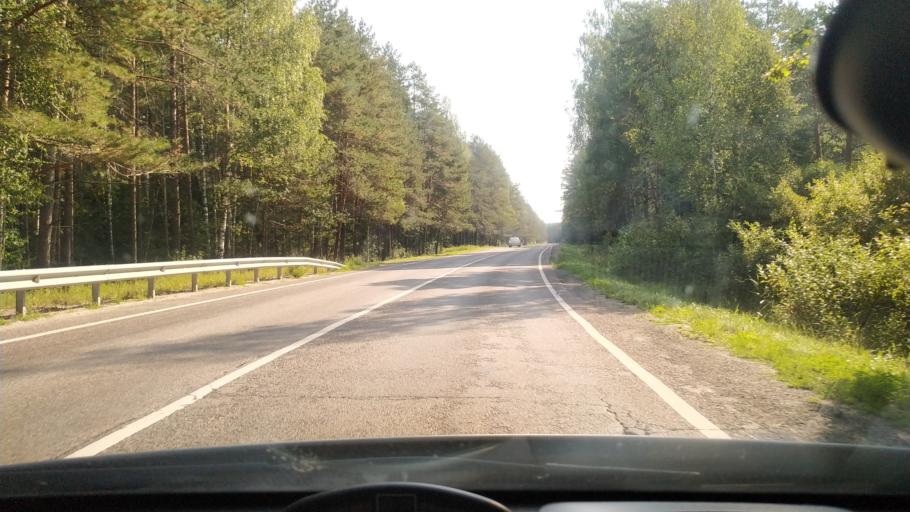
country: RU
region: Moskovskaya
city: Dmitrovskiy Pogost
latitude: 55.2359
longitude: 39.9628
